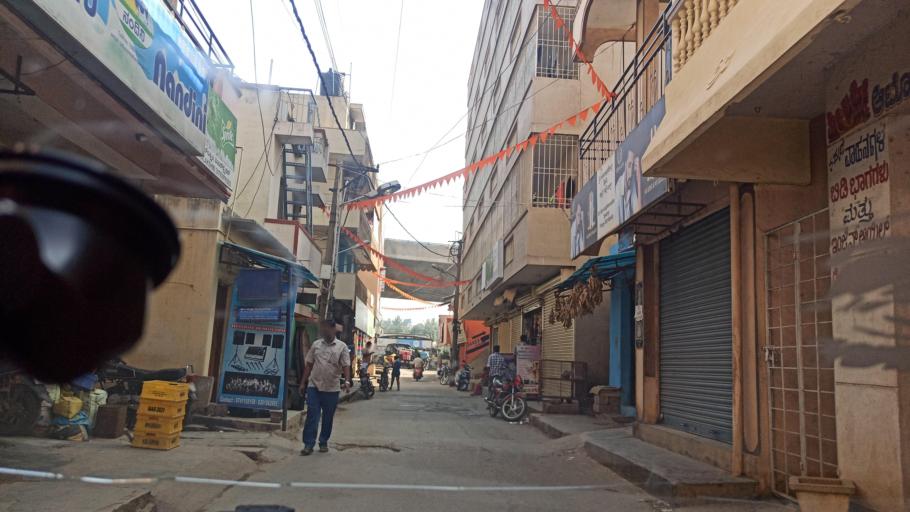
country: IN
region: Karnataka
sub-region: Bangalore Urban
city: Yelahanka
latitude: 13.0662
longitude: 77.5924
